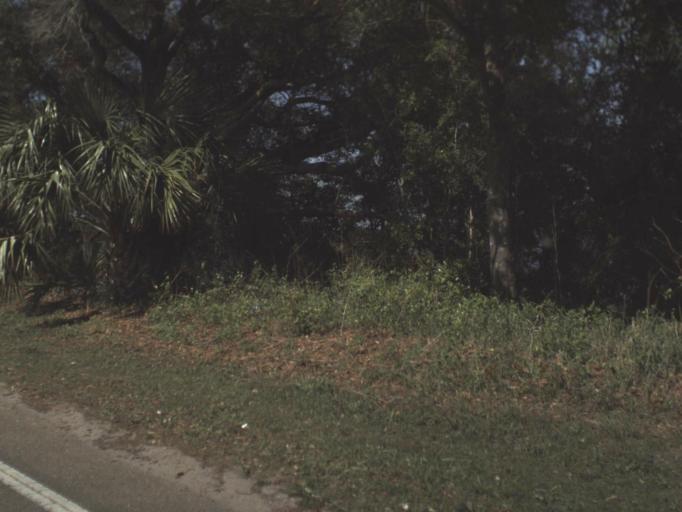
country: US
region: Florida
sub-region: Escambia County
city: East Pensacola Heights
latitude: 30.4380
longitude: -87.1738
